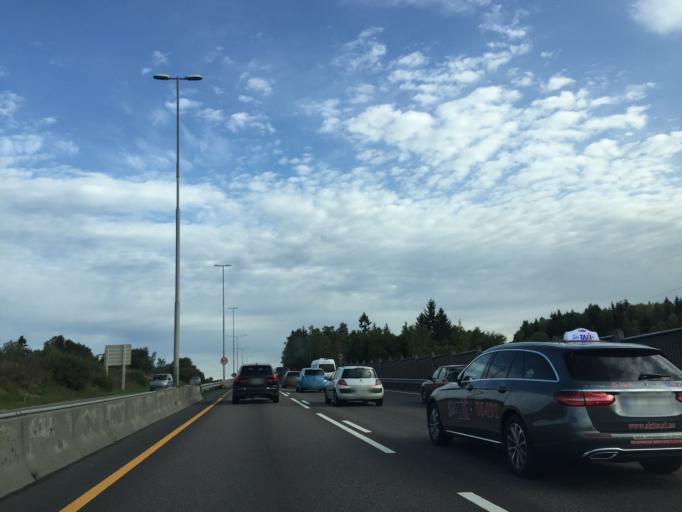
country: NO
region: Akershus
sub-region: Oppegard
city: Kolbotn
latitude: 59.8410
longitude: 10.8391
